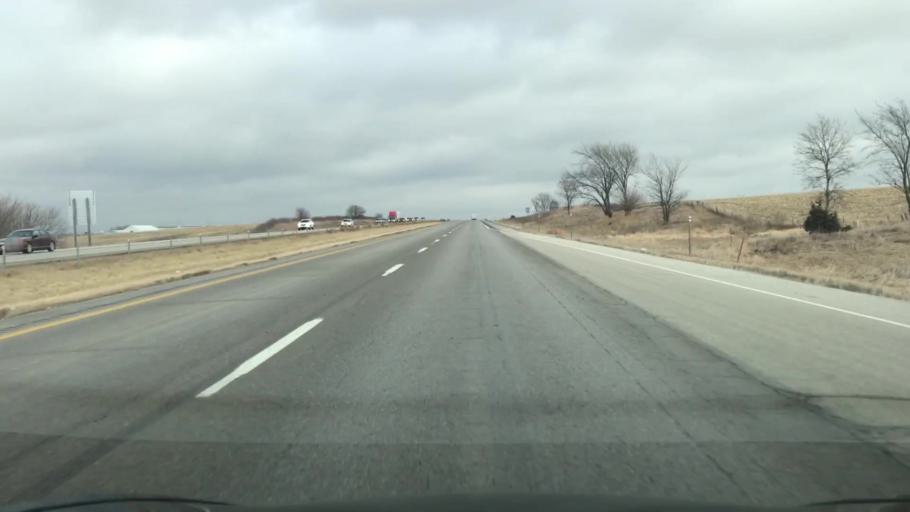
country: US
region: Iowa
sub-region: Guthrie County
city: Stuart
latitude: 41.4958
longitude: -94.4061
